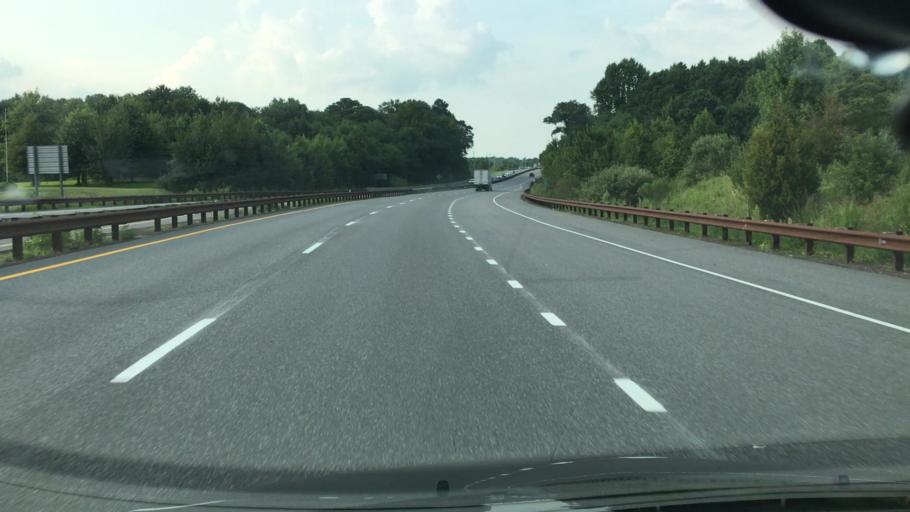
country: US
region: Delaware
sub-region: Sussex County
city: Selbyville
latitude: 38.4069
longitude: -75.2126
